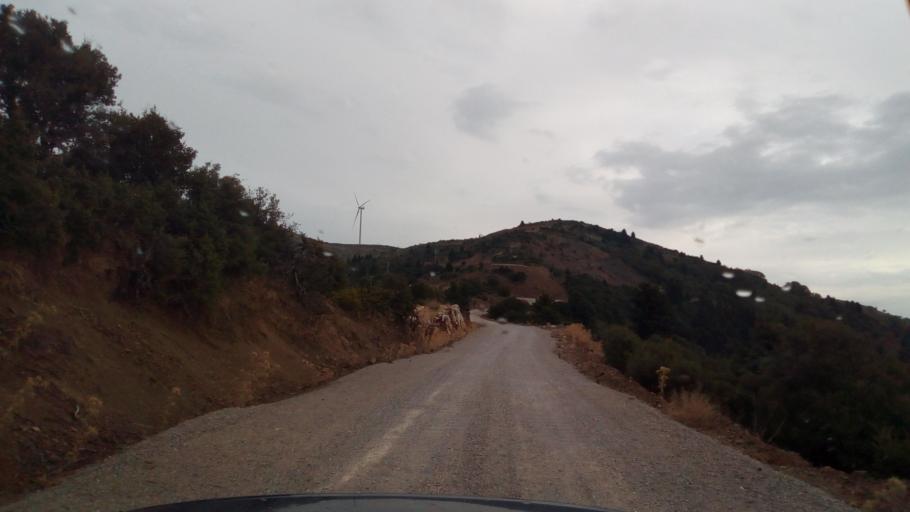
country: GR
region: Central Greece
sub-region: Nomos Fokidos
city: Lidoriki
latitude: 38.4448
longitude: 22.0705
